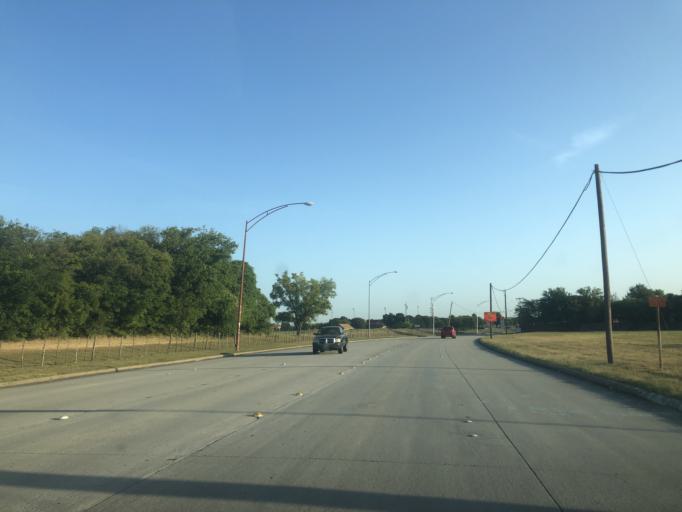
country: US
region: Texas
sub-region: Tarrant County
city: White Settlement
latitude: 32.7225
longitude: -97.5033
